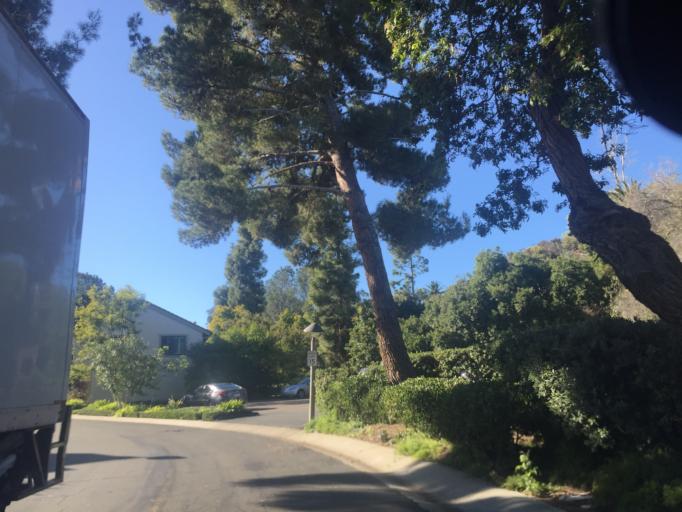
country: US
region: California
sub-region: San Diego County
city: Lemon Grove
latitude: 32.7734
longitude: -117.1025
